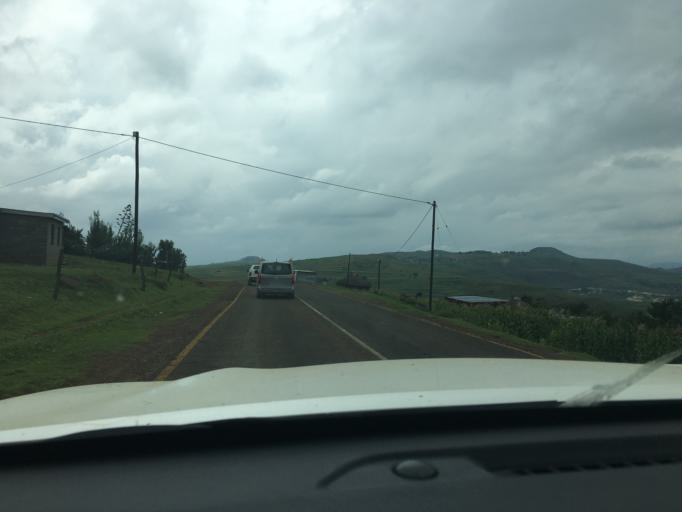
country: LS
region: Berea
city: Teyateyaneng
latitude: -29.2535
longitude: 27.8467
